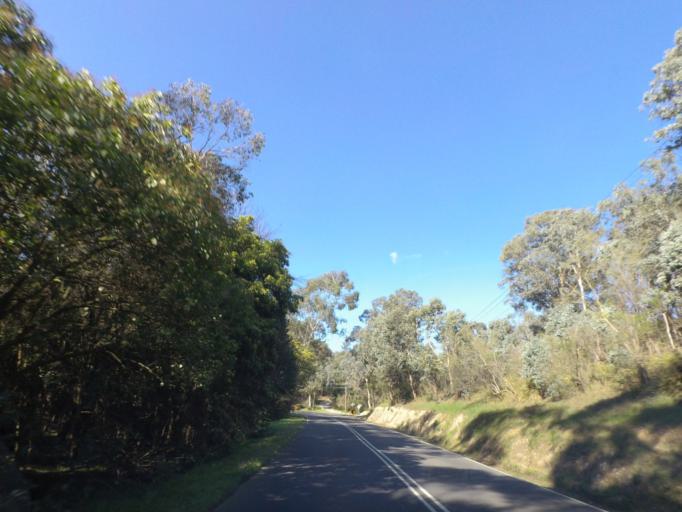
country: AU
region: Victoria
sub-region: Manningham
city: Park Orchards
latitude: -37.7721
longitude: 145.2089
